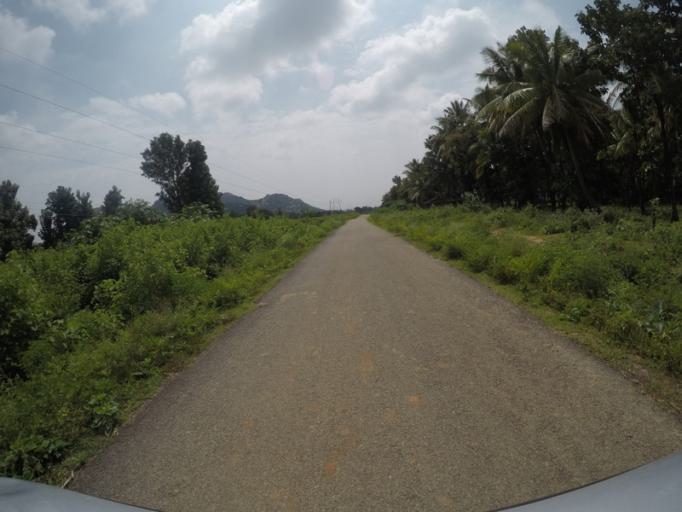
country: IN
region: Karnataka
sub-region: Ramanagara
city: Kanakapura
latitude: 12.4758
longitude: 77.3557
